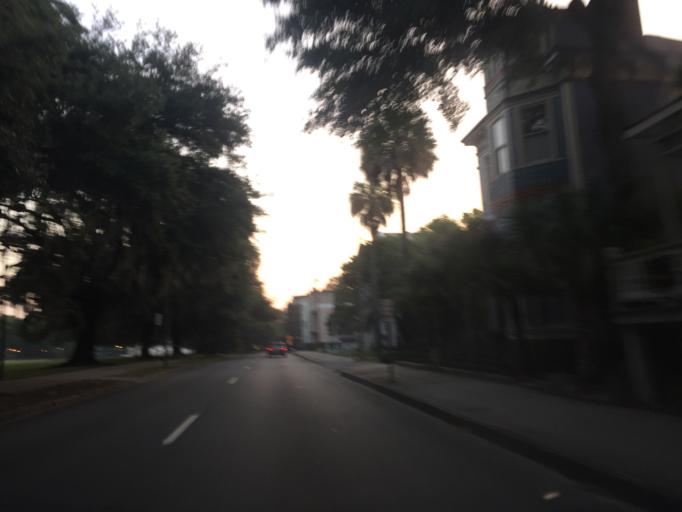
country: US
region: Georgia
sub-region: Chatham County
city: Savannah
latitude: 32.0650
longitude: -81.0959
